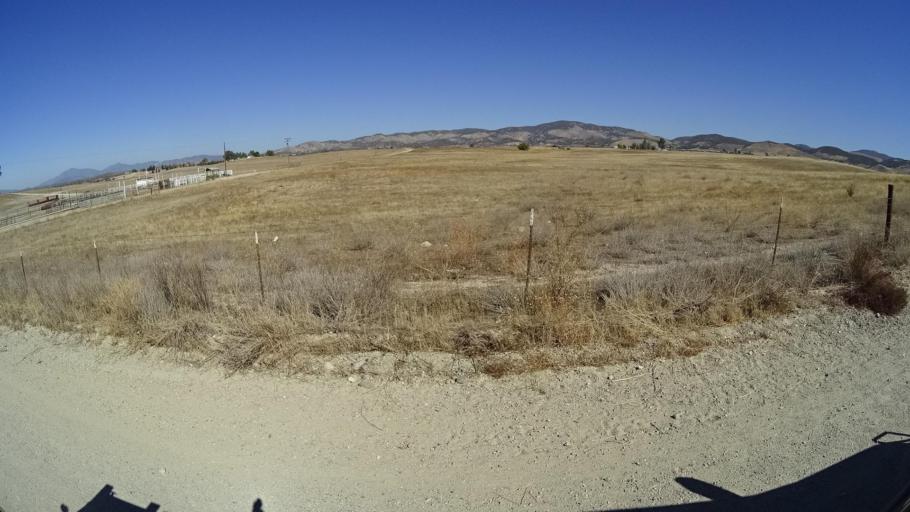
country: US
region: California
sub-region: Monterey County
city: King City
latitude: 35.9513
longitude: -121.0993
